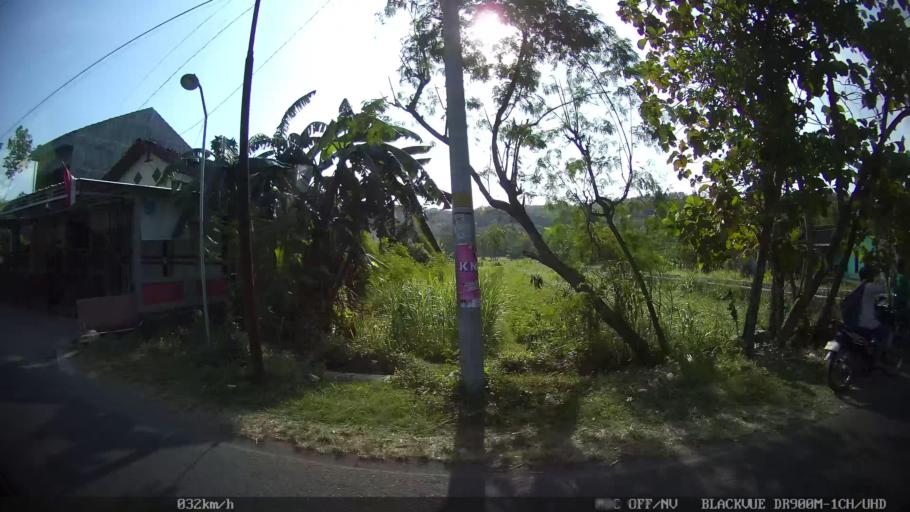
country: ID
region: Daerah Istimewa Yogyakarta
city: Bantul
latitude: -7.8862
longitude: 110.3044
